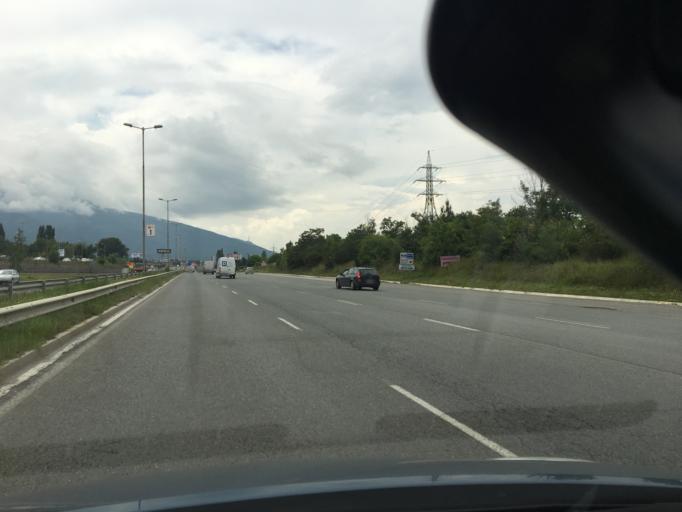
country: BG
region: Sofia-Capital
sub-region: Stolichna Obshtina
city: Sofia
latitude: 42.6237
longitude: 23.3685
